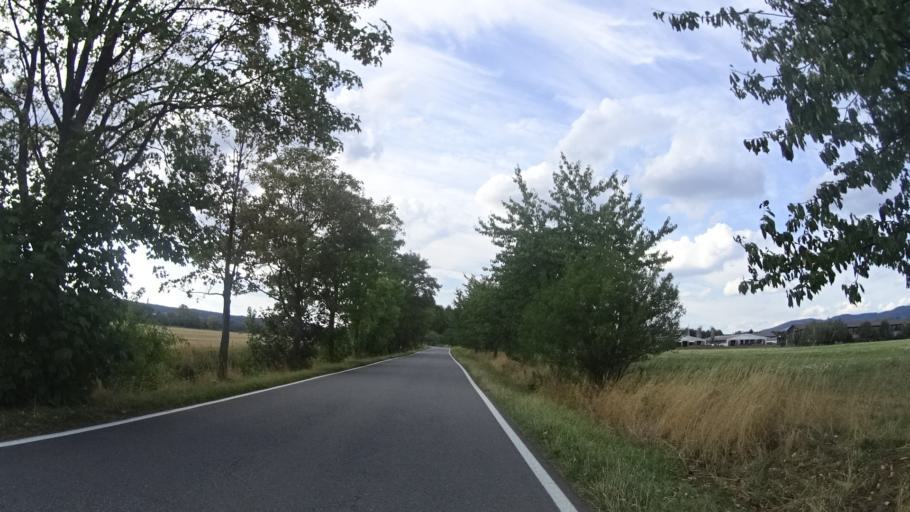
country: CZ
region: Olomoucky
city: Dubicko
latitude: 49.8199
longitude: 16.9388
